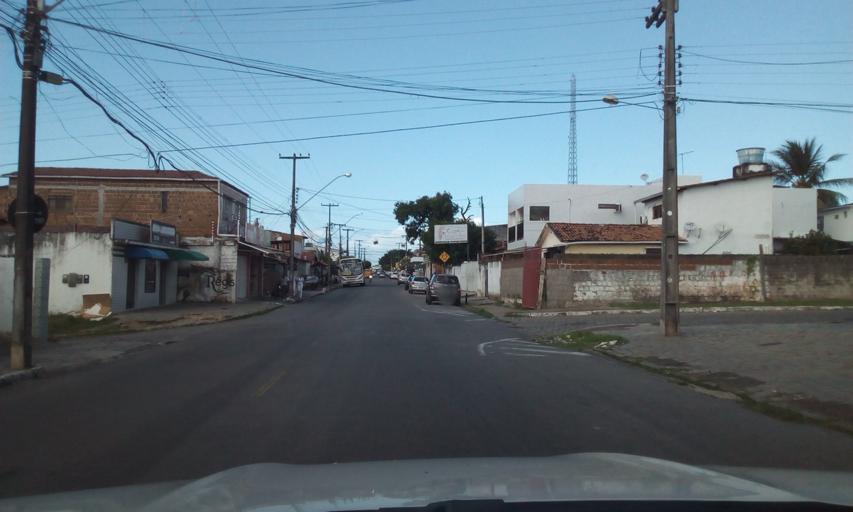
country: BR
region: Paraiba
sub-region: Joao Pessoa
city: Joao Pessoa
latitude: -7.1072
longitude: -34.8607
